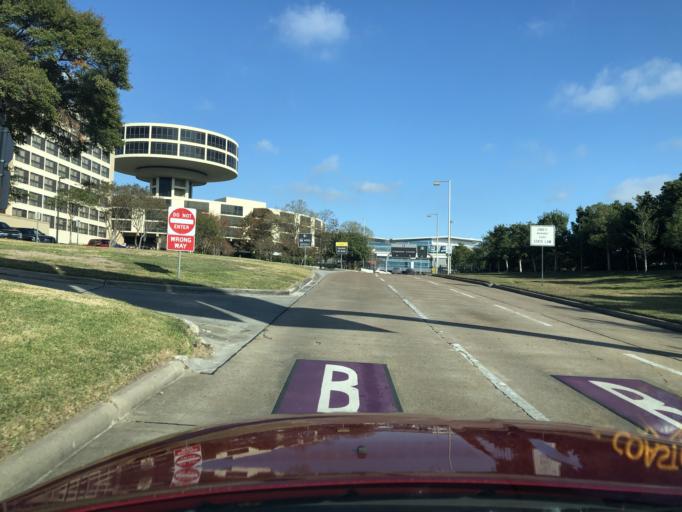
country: US
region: Texas
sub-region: Harris County
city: Aldine
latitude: 29.9852
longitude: -95.3417
